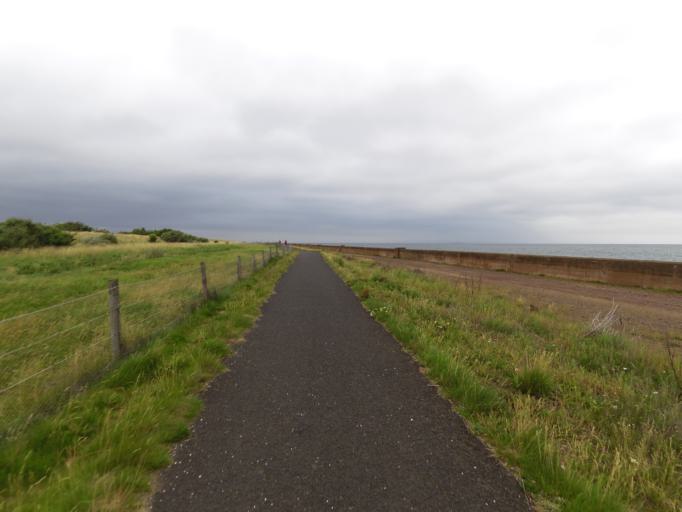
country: GB
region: Scotland
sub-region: East Lothian
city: Musselburgh
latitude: 55.9526
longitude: -3.0274
